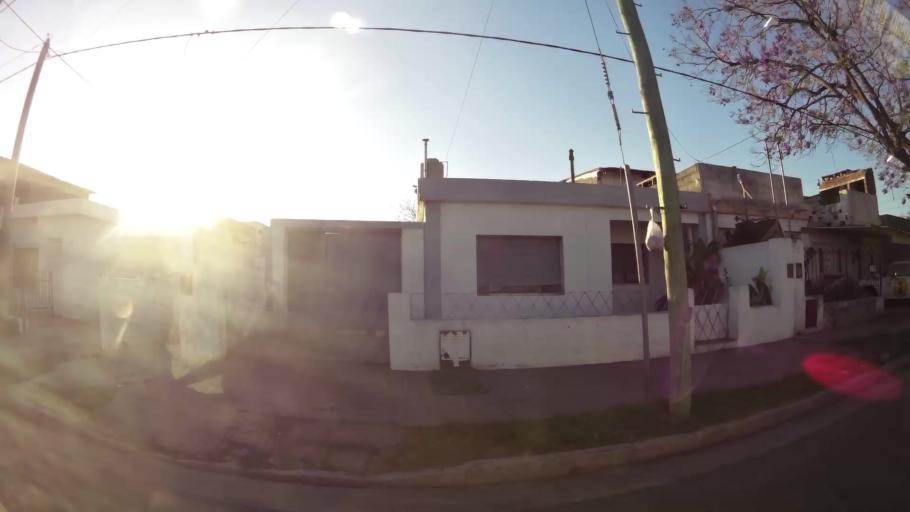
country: AR
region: Cordoba
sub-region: Departamento de Capital
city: Cordoba
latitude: -31.3728
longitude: -64.2000
